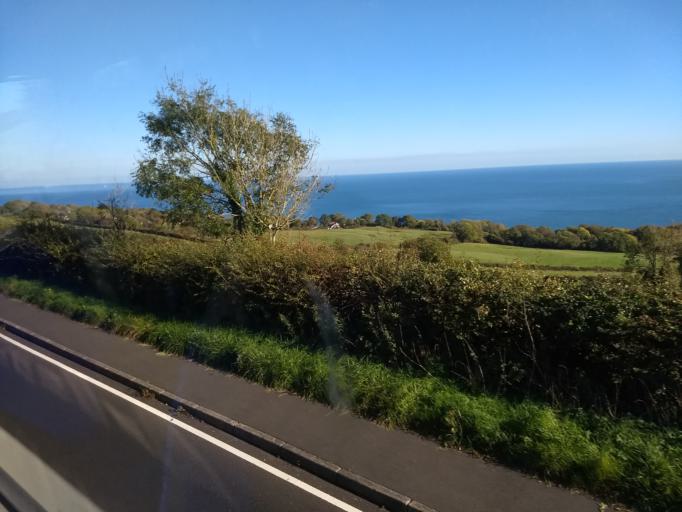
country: GB
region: England
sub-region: Isle of Wight
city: Shanklin
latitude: 50.6142
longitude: -1.1861
